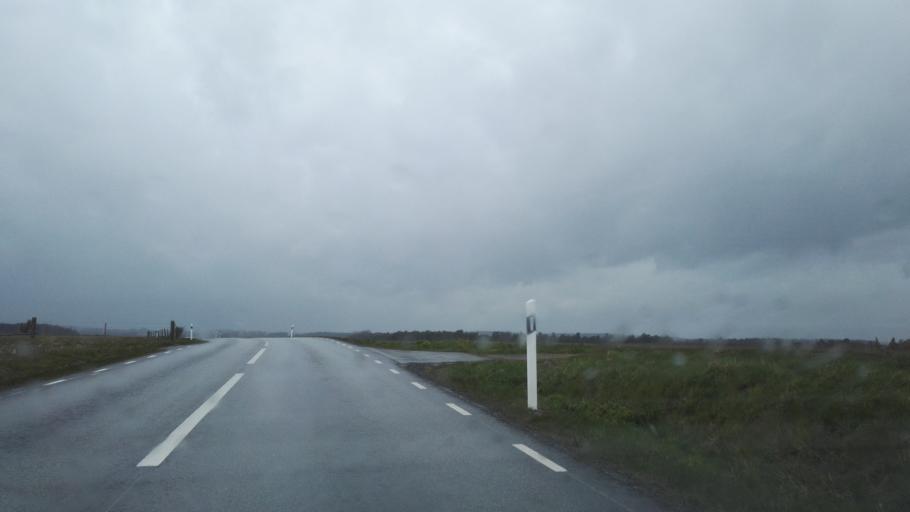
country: SE
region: Skane
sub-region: Simrishamns Kommun
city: Kivik
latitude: 55.7010
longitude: 14.1909
